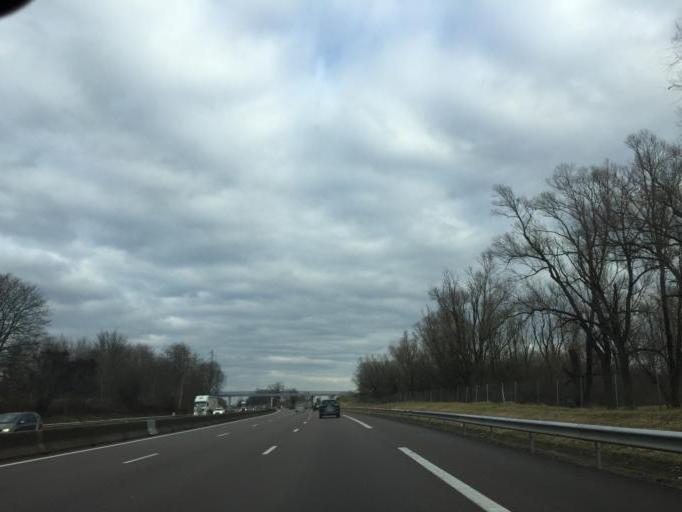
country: FR
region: Bourgogne
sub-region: Departement de Saone-et-Loire
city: Tournus
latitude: 46.5255
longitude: 4.9183
